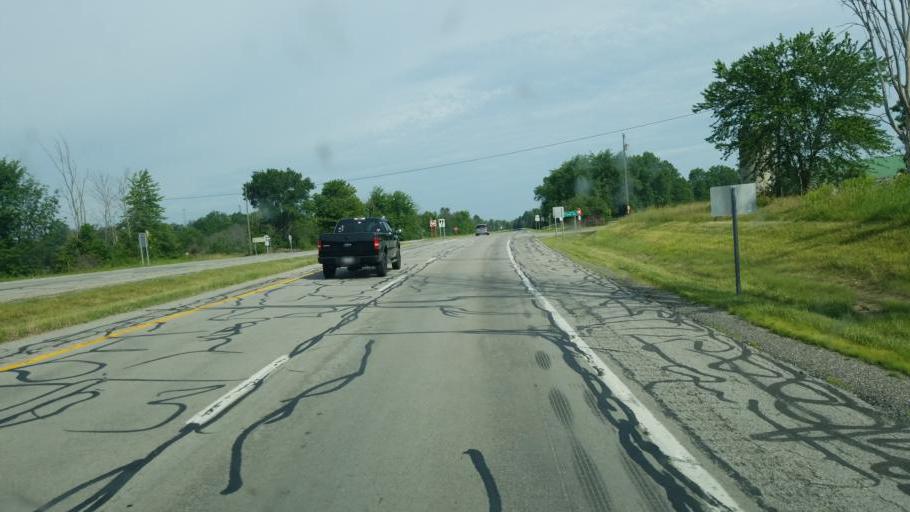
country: US
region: Ohio
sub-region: Medina County
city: Lodi
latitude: 41.0401
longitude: -81.9811
